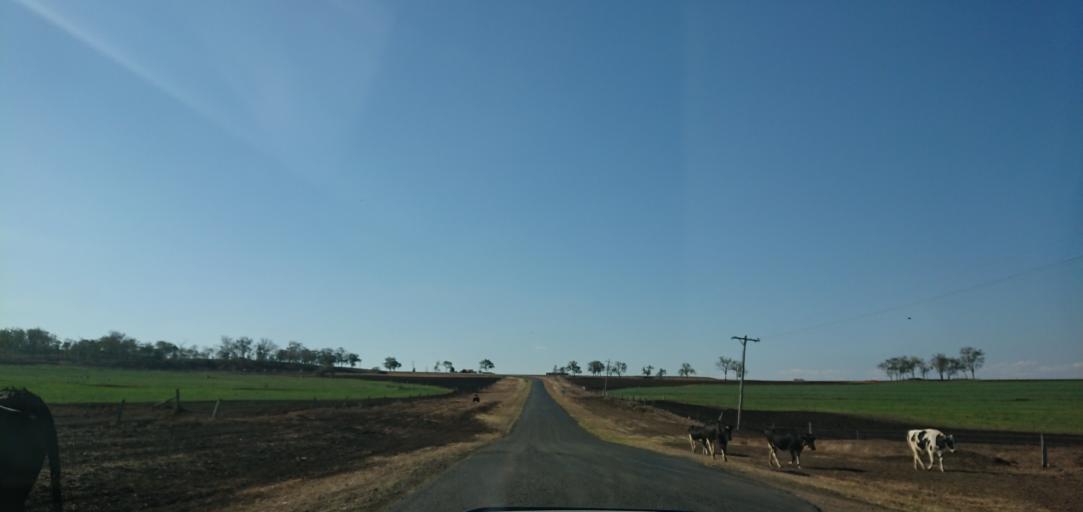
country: AU
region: Queensland
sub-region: Toowoomba
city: Westbrook
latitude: -27.7058
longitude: 151.7165
